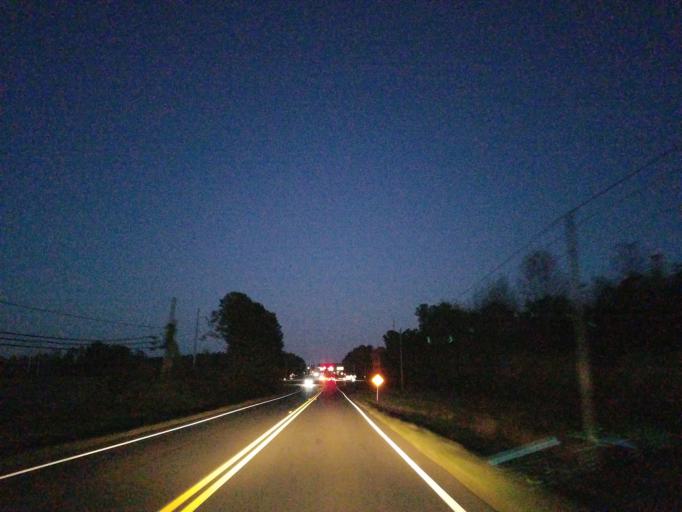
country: US
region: Georgia
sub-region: Forsyth County
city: Cumming
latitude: 34.2512
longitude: -84.0981
